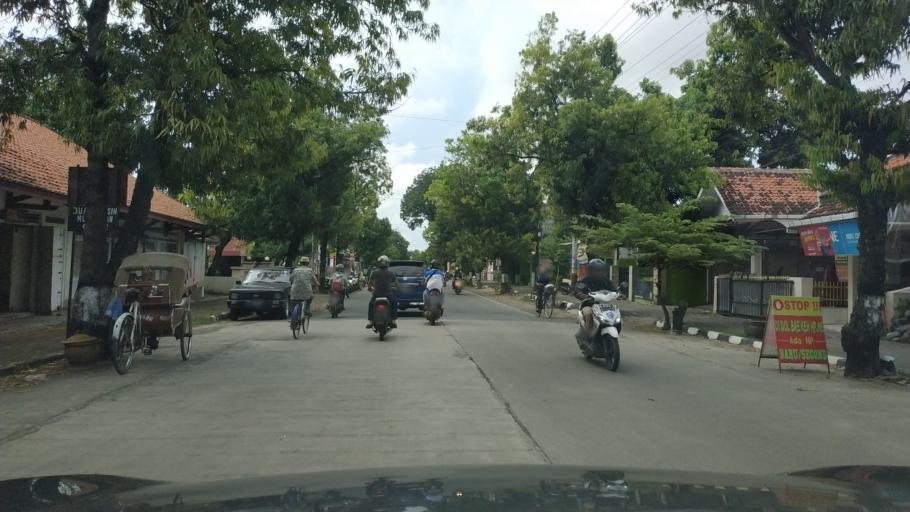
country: ID
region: Central Java
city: Pemalang
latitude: -6.9032
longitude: 109.3833
